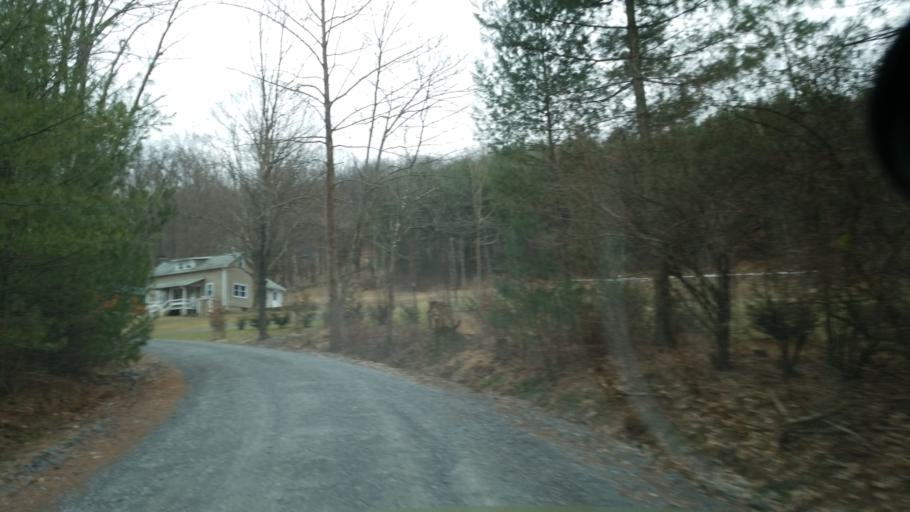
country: US
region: Pennsylvania
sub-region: Centre County
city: Centre Hall
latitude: 40.7686
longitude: -77.6822
